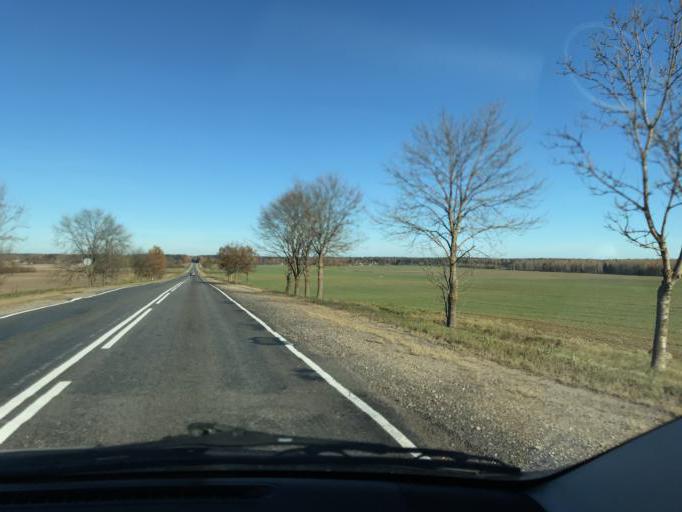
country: BY
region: Vitebsk
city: Lyepyel'
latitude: 55.0428
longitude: 28.7494
